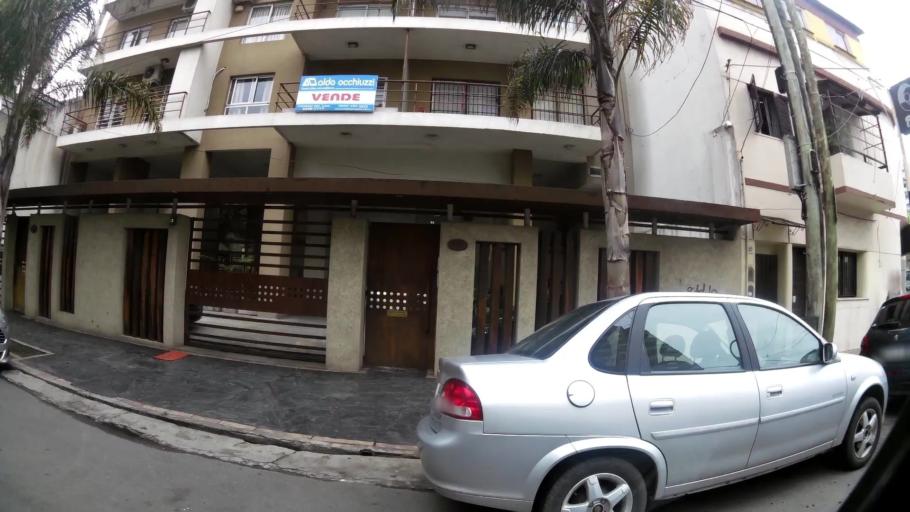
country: AR
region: Buenos Aires
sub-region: Partido de Lanus
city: Lanus
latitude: -34.7084
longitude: -58.3858
